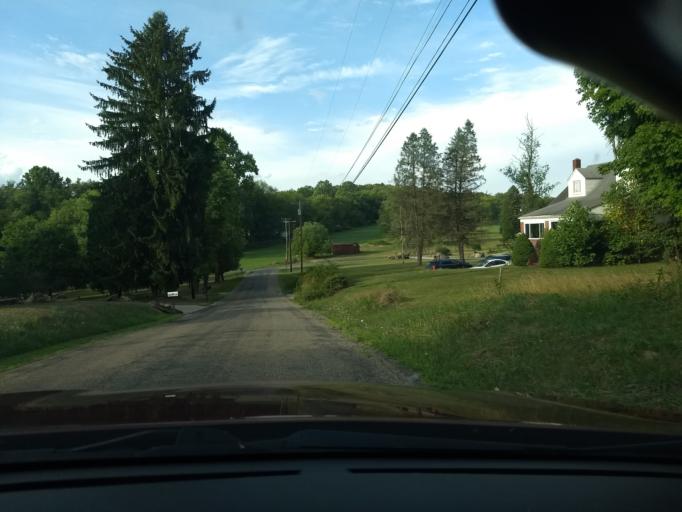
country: US
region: Pennsylvania
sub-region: Armstrong County
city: Freeport
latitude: 40.6656
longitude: -79.6639
